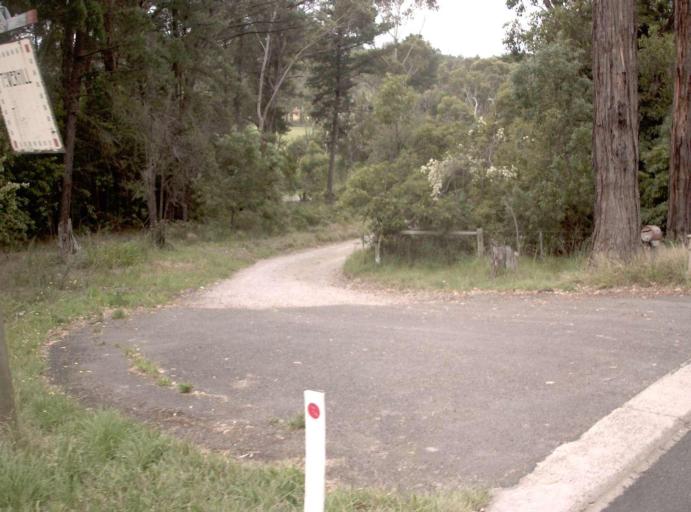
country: AU
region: Victoria
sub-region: Yarra Ranges
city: Mount Evelyn
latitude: -37.7556
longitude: 145.3841
